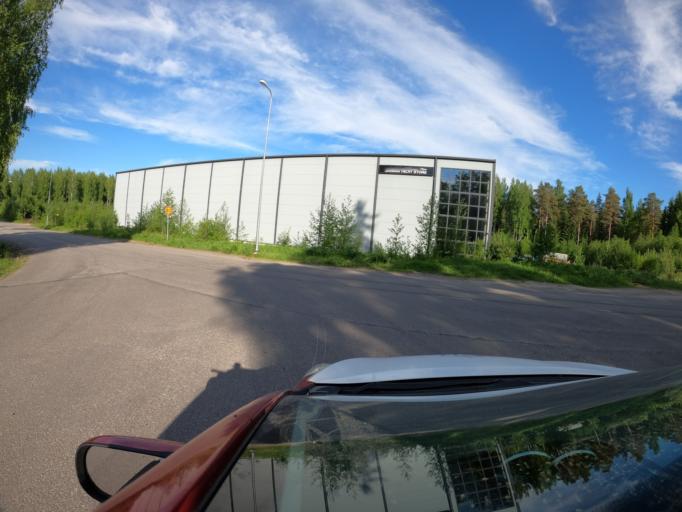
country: FI
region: Southern Savonia
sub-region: Savonlinna
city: Savonlinna
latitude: 61.8443
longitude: 28.9539
